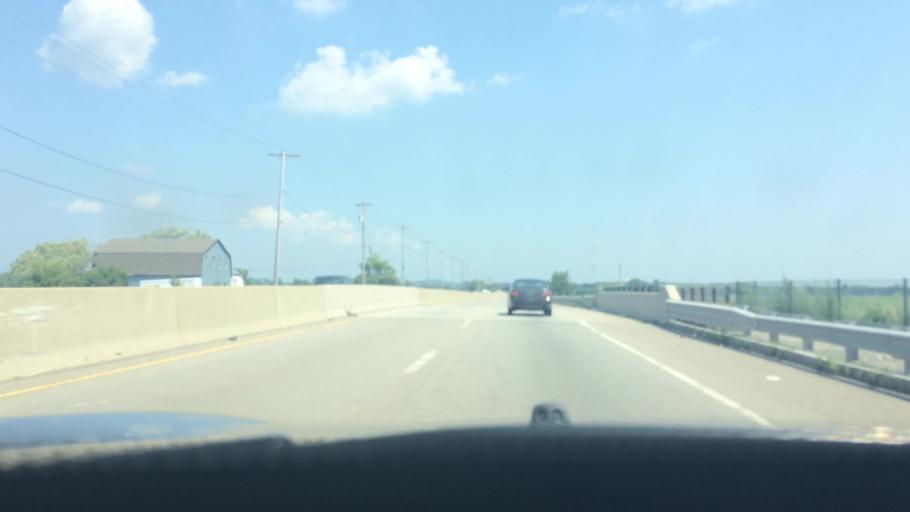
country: US
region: Massachusetts
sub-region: Suffolk County
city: Revere
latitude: 42.4280
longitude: -70.9995
